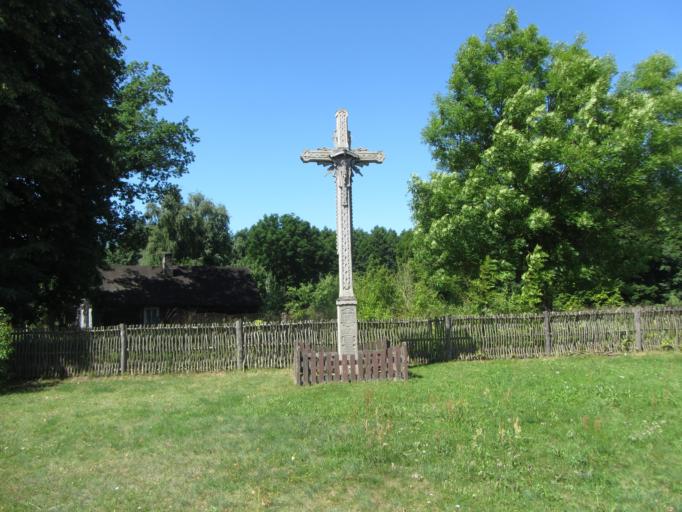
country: LT
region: Vilnius County
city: Elektrenai
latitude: 54.8368
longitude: 24.5736
